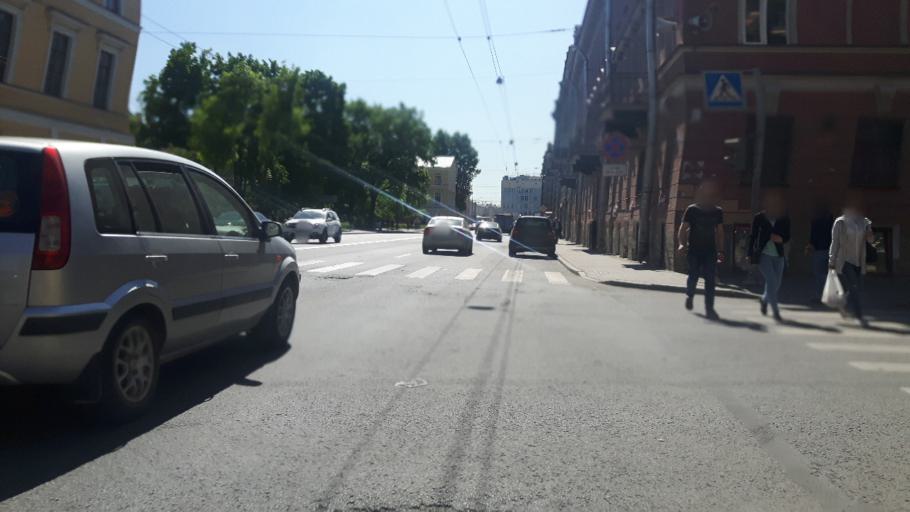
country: RU
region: St.-Petersburg
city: Admiralteisky
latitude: 59.9116
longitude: 30.2975
